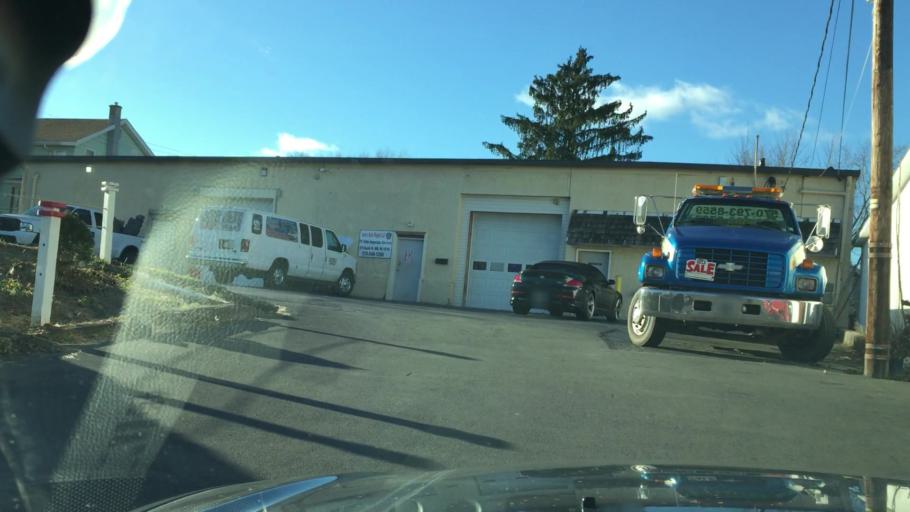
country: US
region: Pennsylvania
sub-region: Luzerne County
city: Ashley
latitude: 41.2275
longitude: -75.8932
